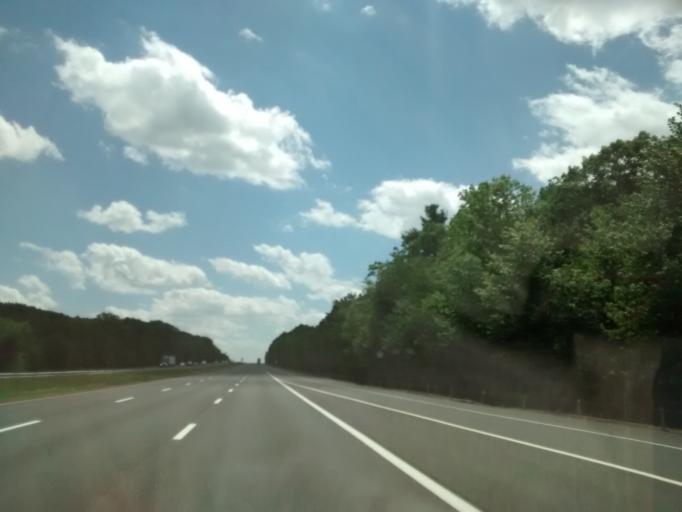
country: US
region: Massachusetts
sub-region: Hampden County
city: Holland
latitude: 41.9739
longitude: -72.1843
